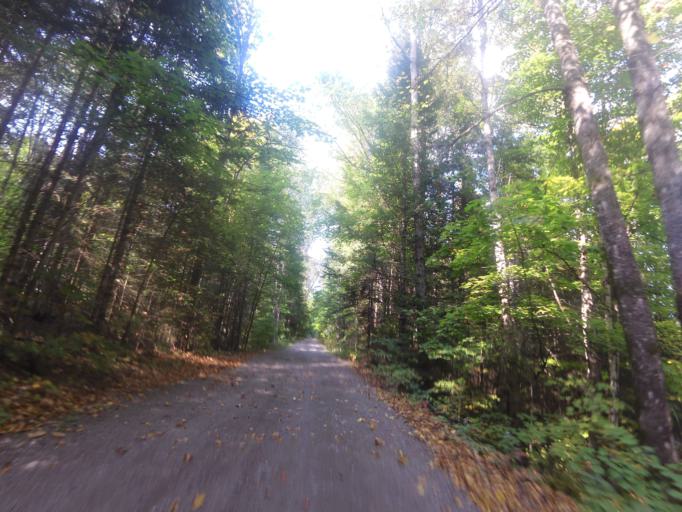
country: CA
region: Ontario
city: Renfrew
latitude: 45.1398
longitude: -76.6861
